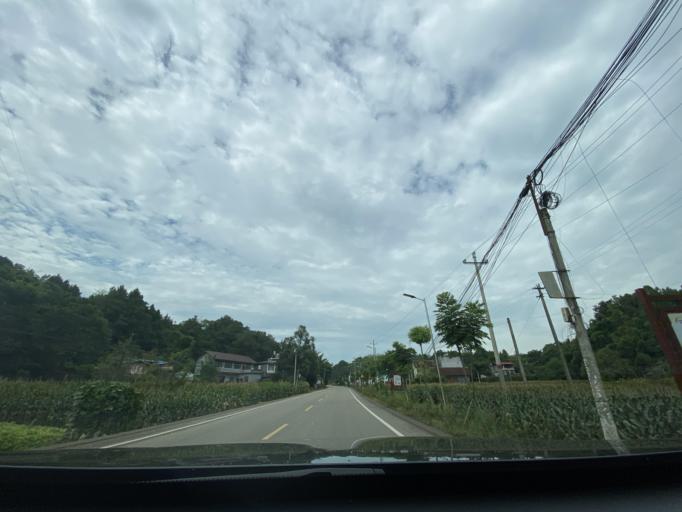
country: CN
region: Sichuan
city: Jiancheng
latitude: 30.4783
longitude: 104.6309
